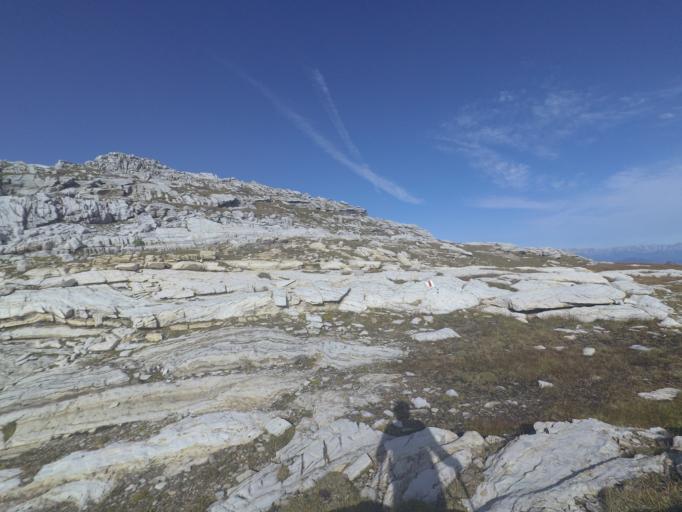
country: AT
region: Salzburg
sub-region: Politischer Bezirk Sankt Johann im Pongau
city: Kleinarl
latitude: 47.2226
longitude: 13.4076
